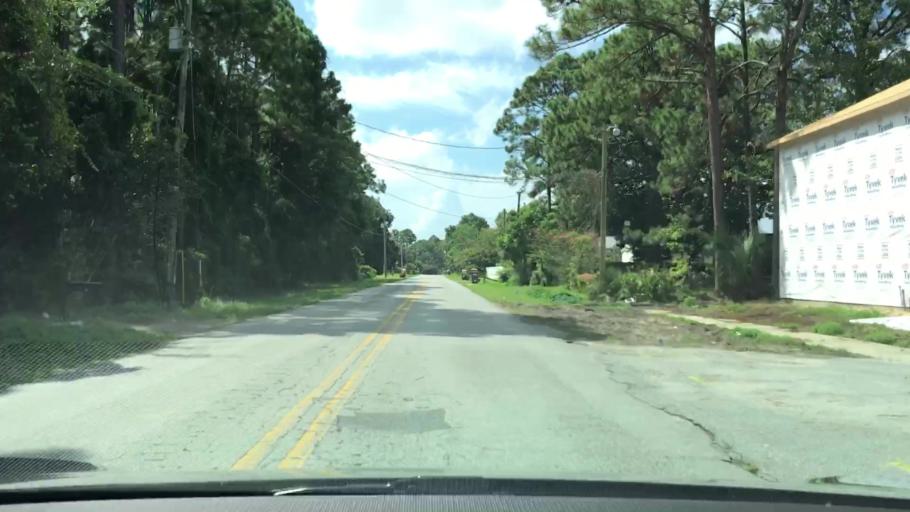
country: US
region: Florida
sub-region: Bay County
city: Panama City Beach
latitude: 30.1738
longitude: -85.7865
